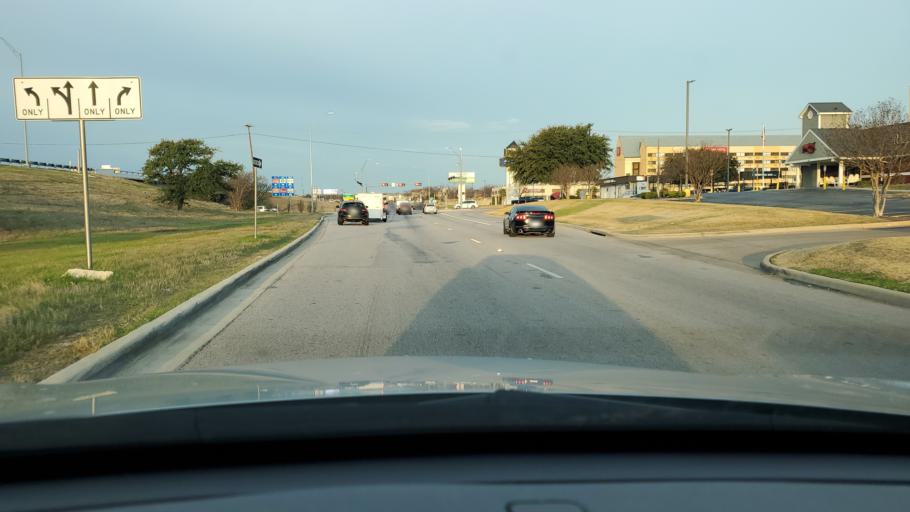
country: US
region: Texas
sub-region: Bell County
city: Killeen
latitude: 31.0948
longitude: -97.7308
